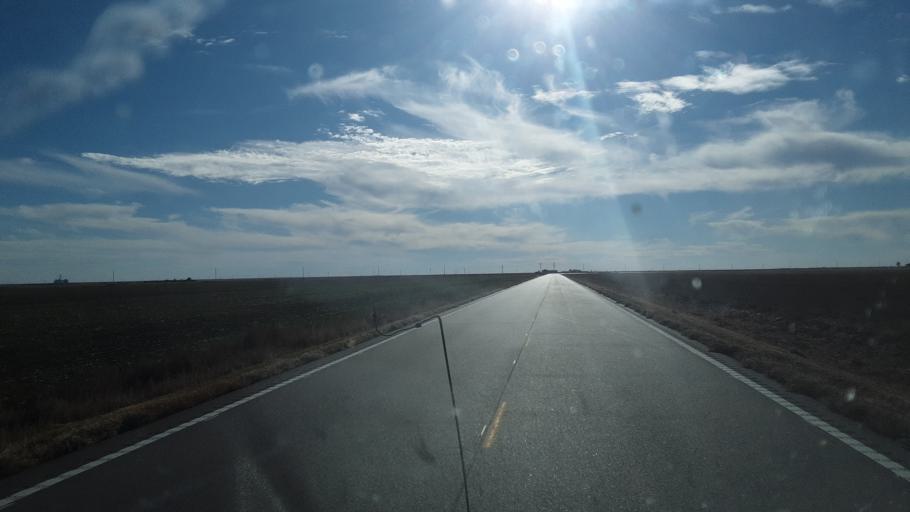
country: US
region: Kansas
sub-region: Gray County
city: Cimarron
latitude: 38.0637
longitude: -100.2195
